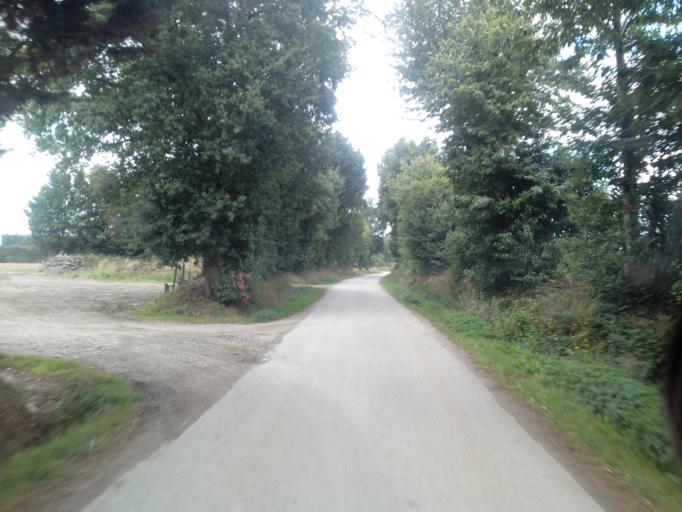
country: FR
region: Brittany
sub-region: Departement du Morbihan
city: Meneac
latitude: 48.1238
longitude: -2.4345
